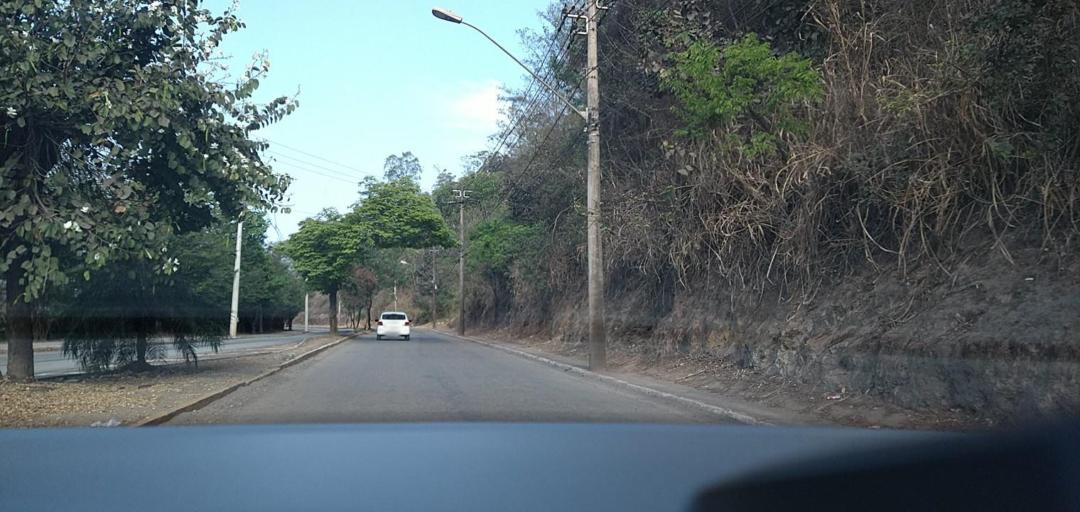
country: BR
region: Minas Gerais
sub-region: Joao Monlevade
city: Joao Monlevade
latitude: -19.8189
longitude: -43.1447
